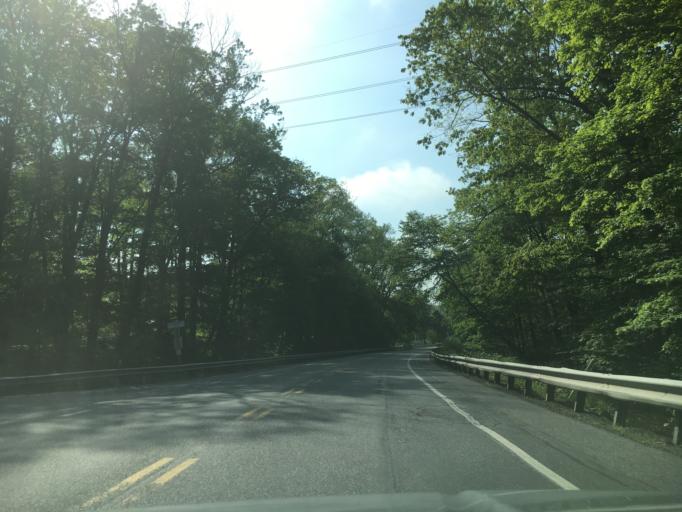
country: US
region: Pennsylvania
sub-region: Berks County
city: New Berlinville
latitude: 40.3614
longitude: -75.6684
